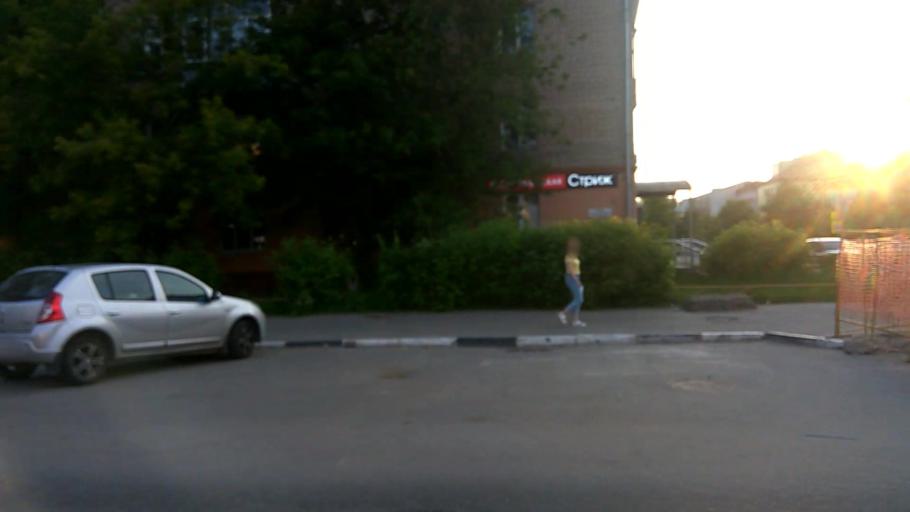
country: RU
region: Moskovskaya
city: Korolev
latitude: 55.9188
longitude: 37.8133
